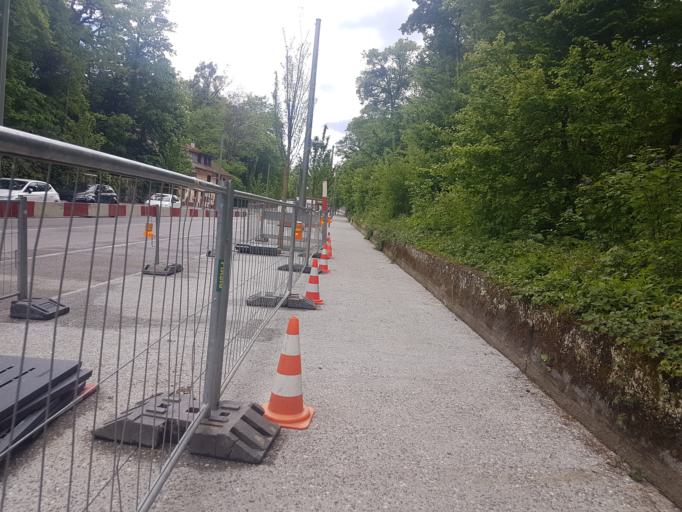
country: CH
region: Geneva
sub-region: Geneva
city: Versoix
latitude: 46.2951
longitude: 6.1668
